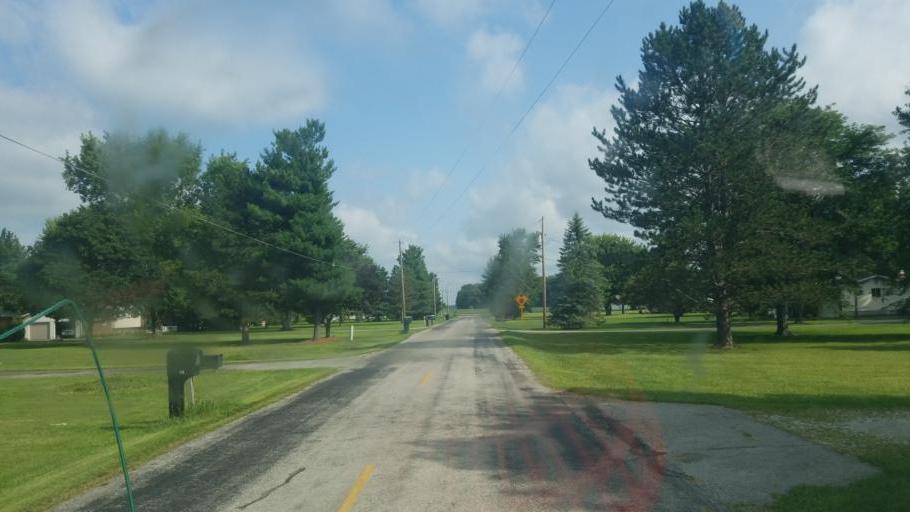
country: US
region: Ohio
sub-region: Marion County
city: Marion
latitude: 40.5992
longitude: -82.9982
